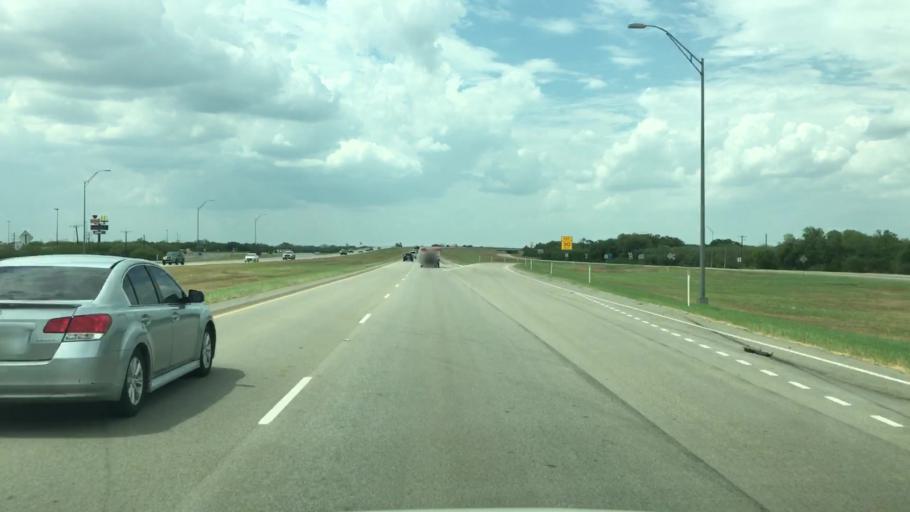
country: US
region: Texas
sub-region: Live Oak County
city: Three Rivers
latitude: 28.5195
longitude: -98.1793
